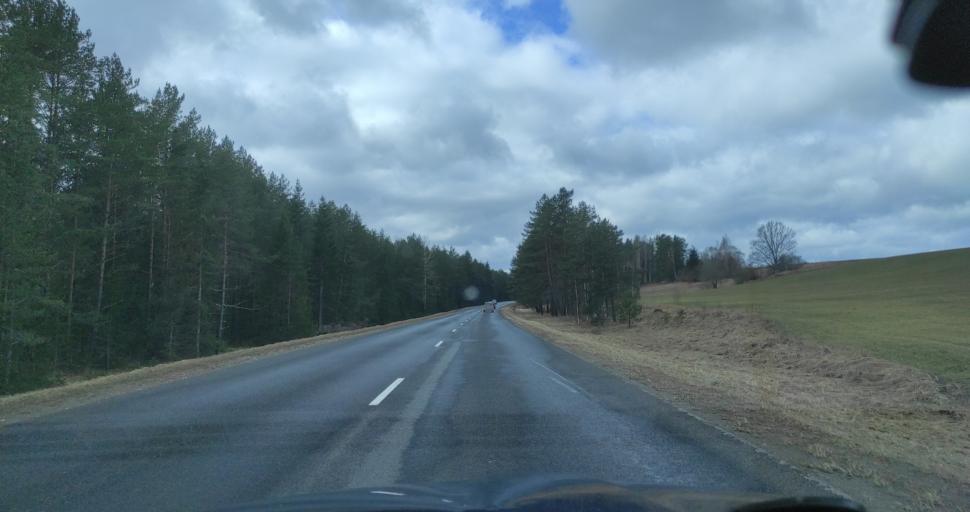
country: LV
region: Talsu Rajons
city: Stende
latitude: 57.0827
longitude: 22.4475
